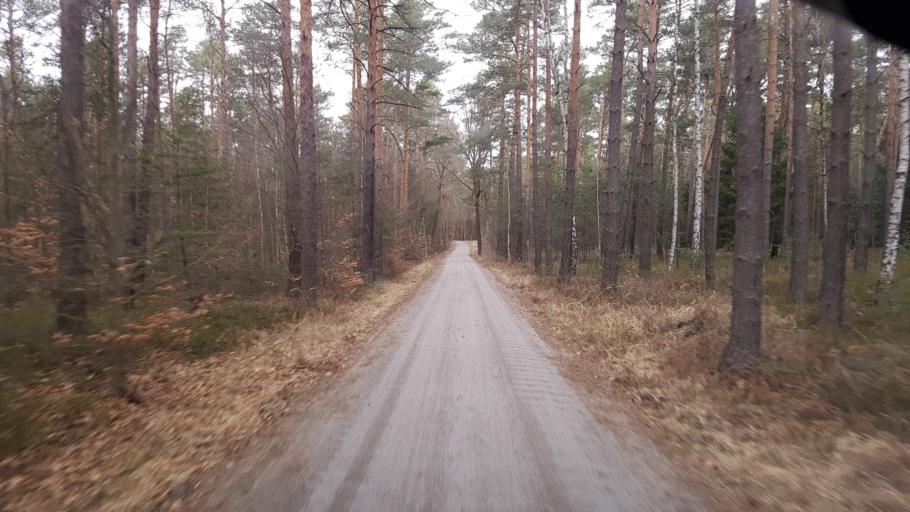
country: DE
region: Brandenburg
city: Finsterwalde
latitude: 51.5749
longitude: 13.7031
